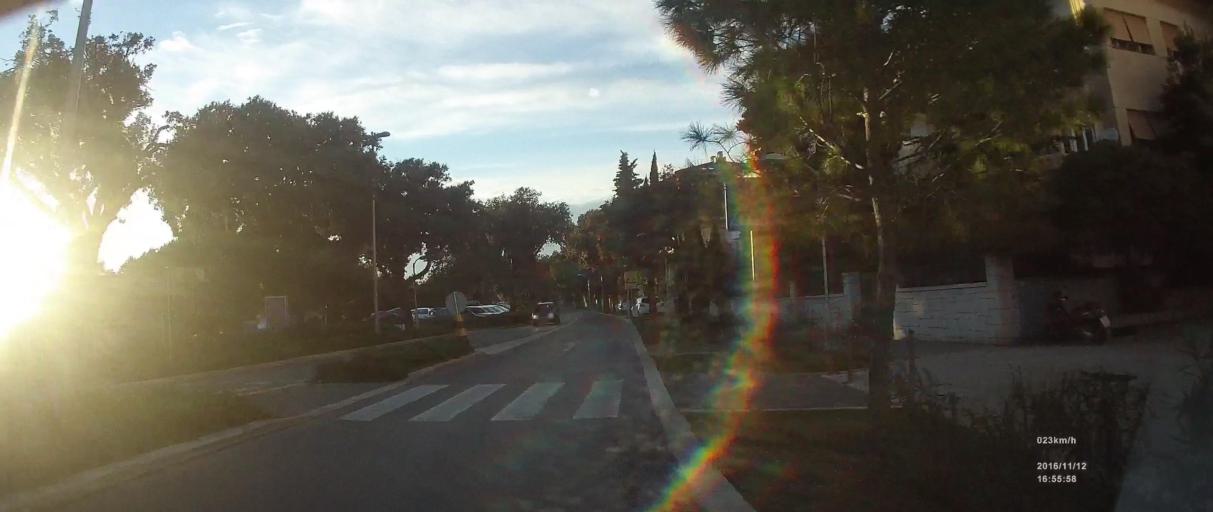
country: HR
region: Splitsko-Dalmatinska
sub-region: Grad Split
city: Split
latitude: 43.5033
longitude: 16.4268
